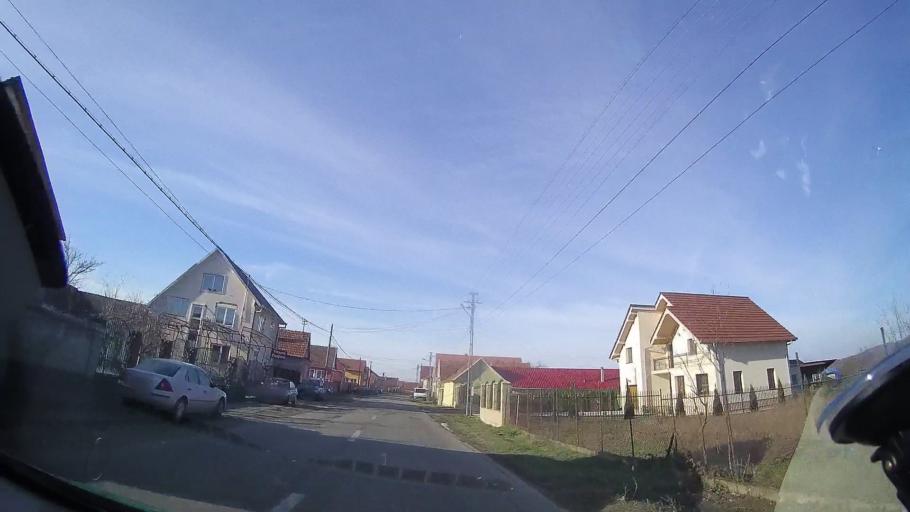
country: RO
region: Bihor
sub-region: Comuna Astileu
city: Astileu
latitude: 47.0293
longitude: 22.3900
